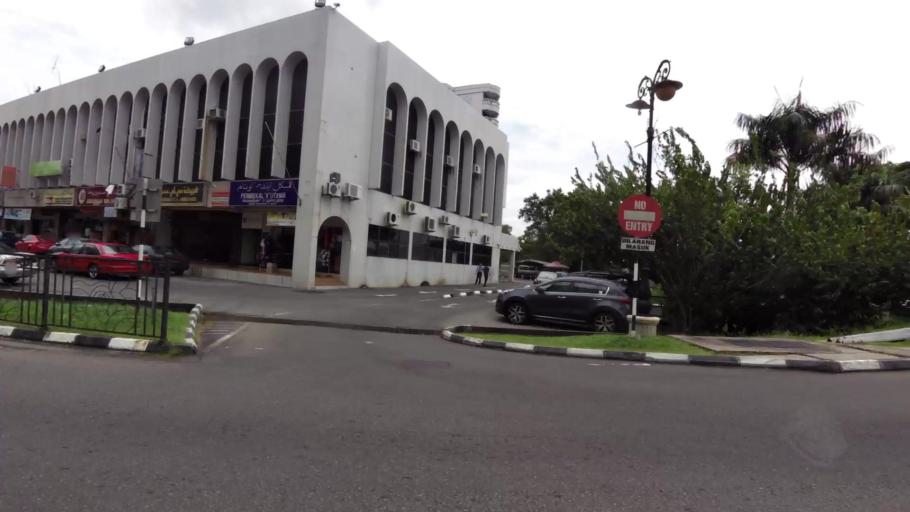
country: BN
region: Brunei and Muara
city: Bandar Seri Begawan
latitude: 4.9058
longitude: 114.9177
